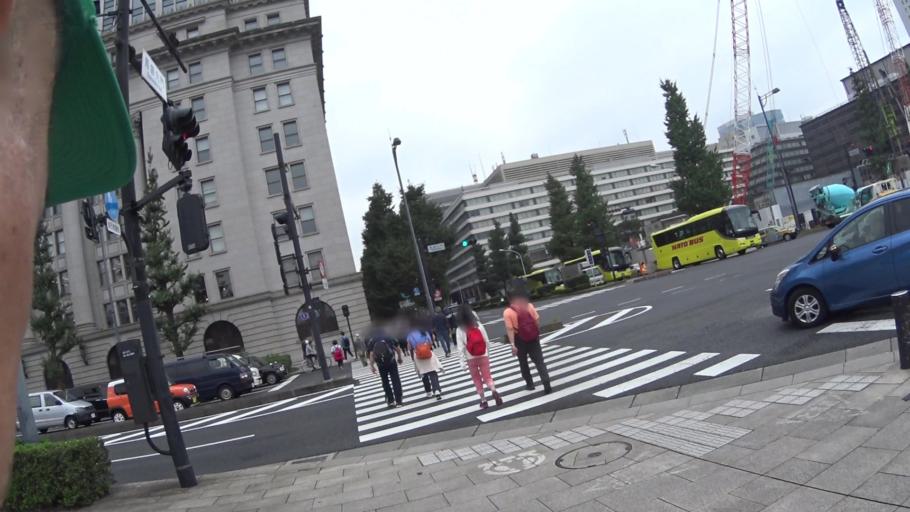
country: JP
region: Tokyo
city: Tokyo
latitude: 35.6787
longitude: 139.7609
